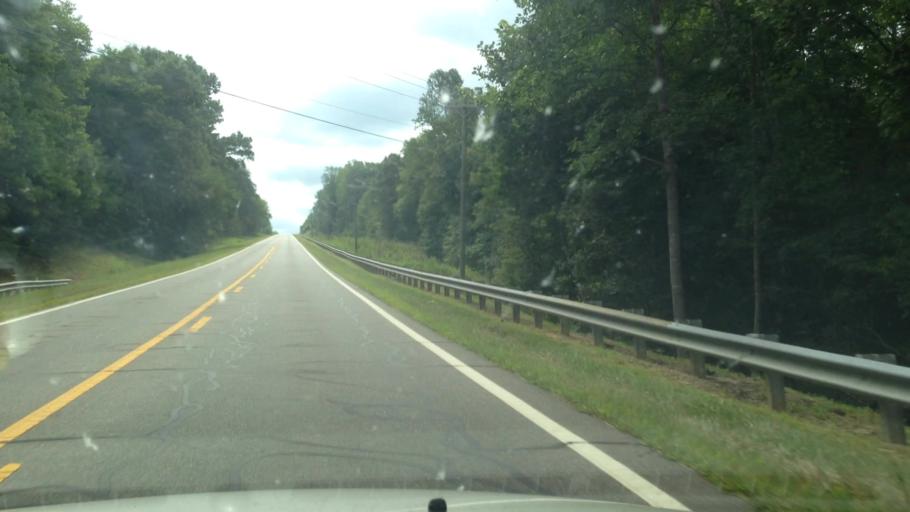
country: US
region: North Carolina
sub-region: Rockingham County
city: Madison
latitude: 36.3816
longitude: -79.9070
